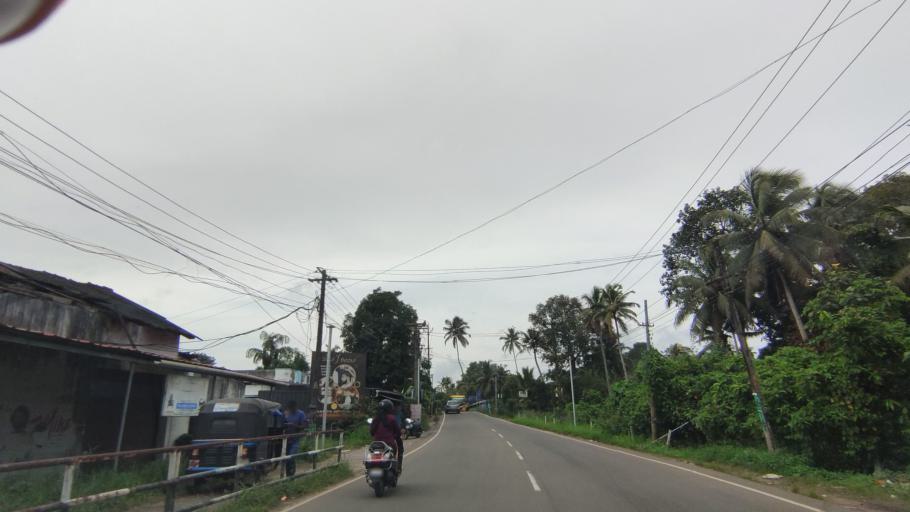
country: IN
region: Kerala
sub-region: Kottayam
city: Kottayam
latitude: 9.6247
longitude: 76.5124
